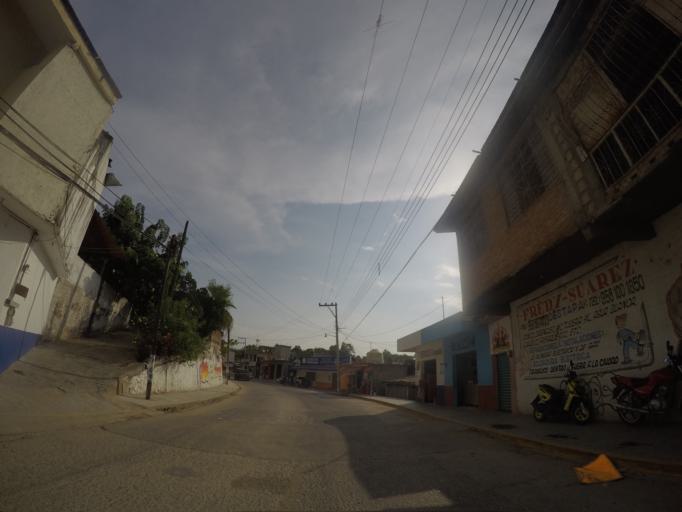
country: MX
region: Oaxaca
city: San Pedro Pochutla
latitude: 15.7503
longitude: -96.4650
